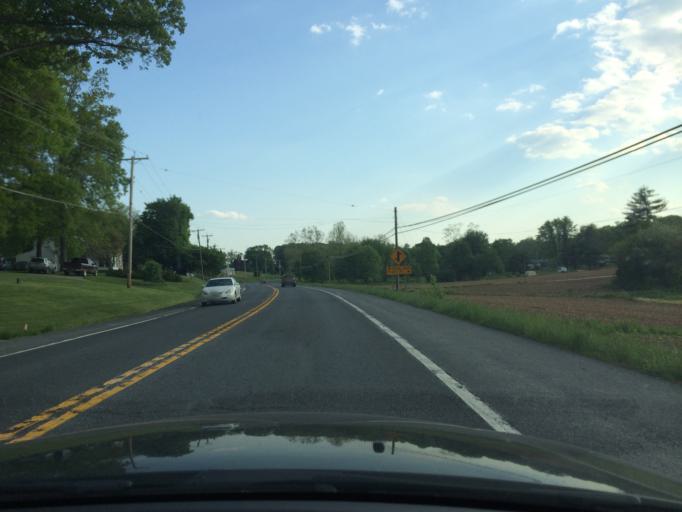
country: US
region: Maryland
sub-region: Carroll County
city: Westminster
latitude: 39.5317
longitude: -77.0233
